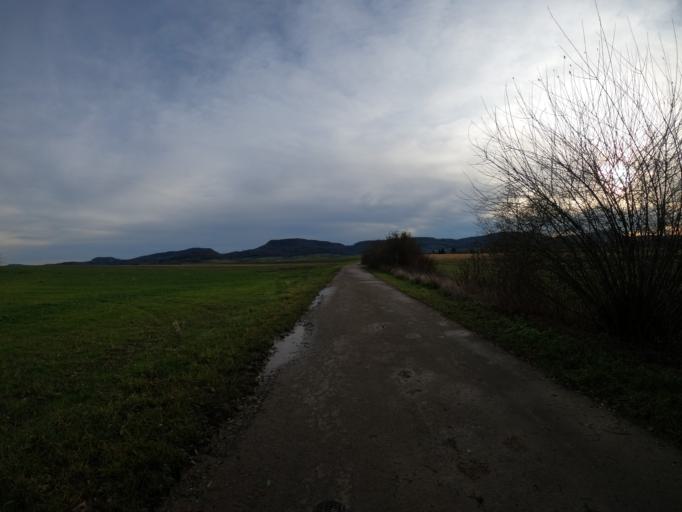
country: DE
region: Baden-Wuerttemberg
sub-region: Regierungsbezirk Stuttgart
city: Heiningen
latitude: 48.6737
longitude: 9.6492
